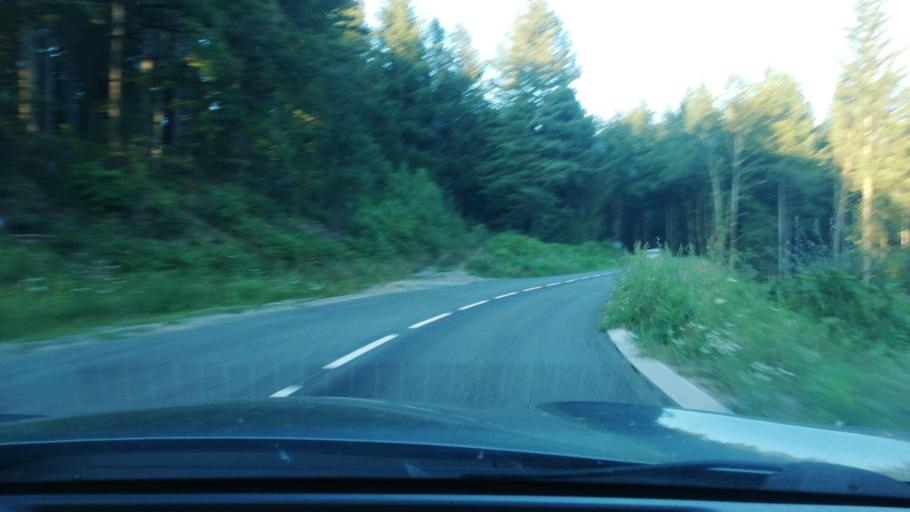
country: FR
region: Auvergne
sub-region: Departement du Cantal
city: Laroquebrou
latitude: 44.9167
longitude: 2.0598
